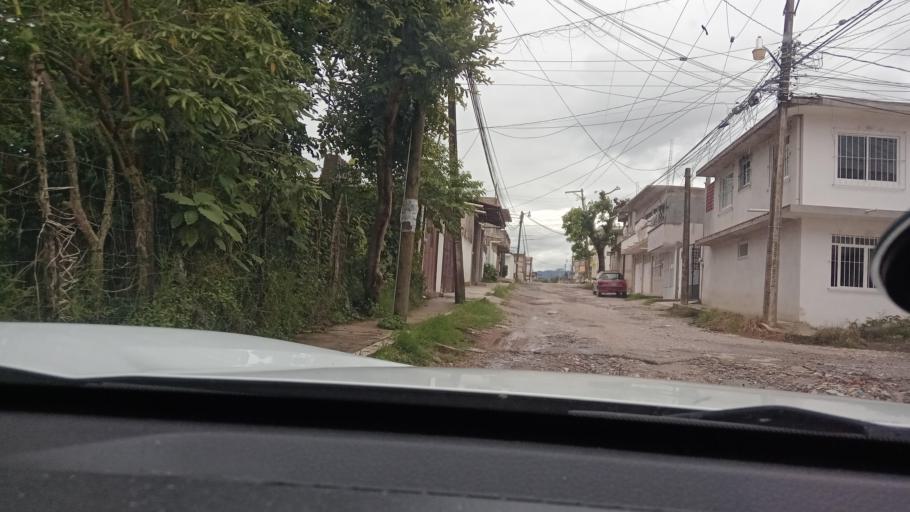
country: MX
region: Veracruz
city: Coatepec
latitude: 19.4433
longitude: -96.9692
